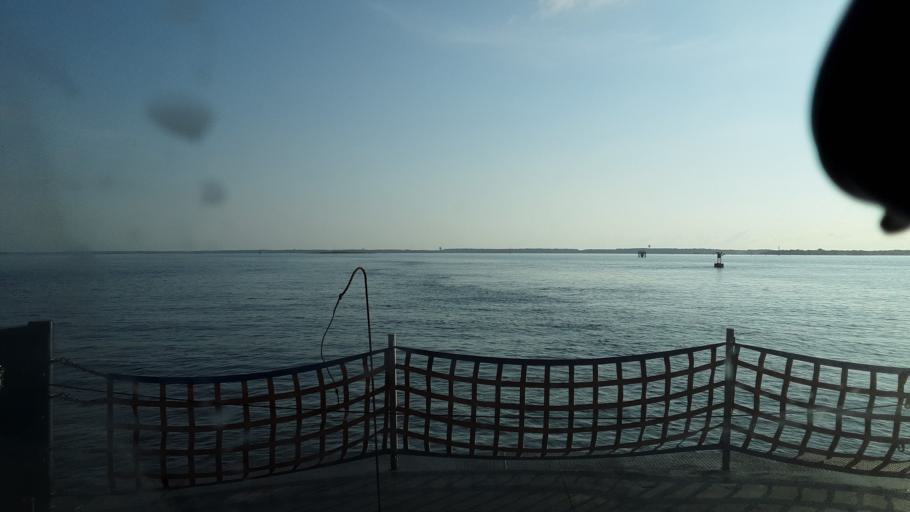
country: US
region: North Carolina
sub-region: New Hanover County
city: Kure Beach
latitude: 33.9588
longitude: -77.9550
